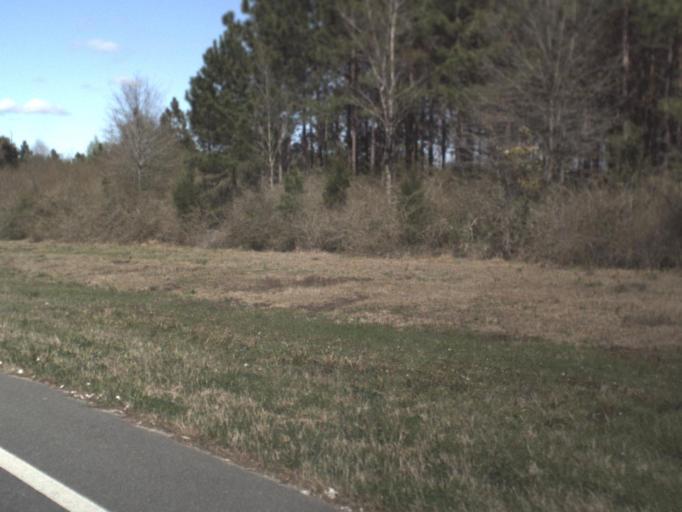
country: US
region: Florida
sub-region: Gadsden County
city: Gretna
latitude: 30.6388
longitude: -84.6753
